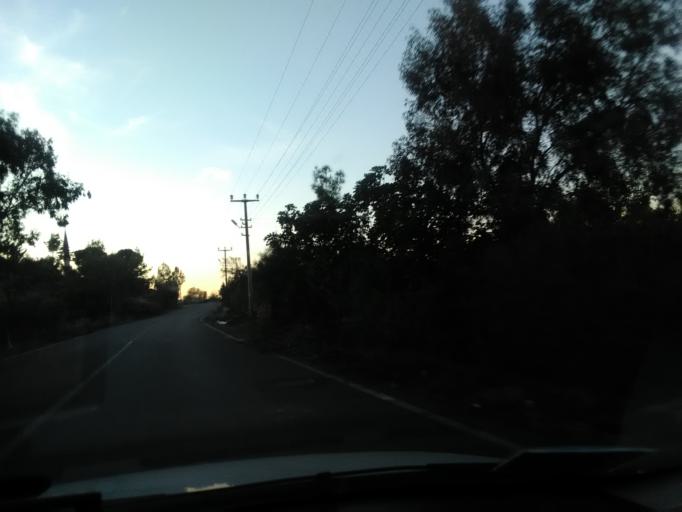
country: TR
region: Antalya
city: Gazipasa
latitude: 36.2581
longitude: 32.3212
